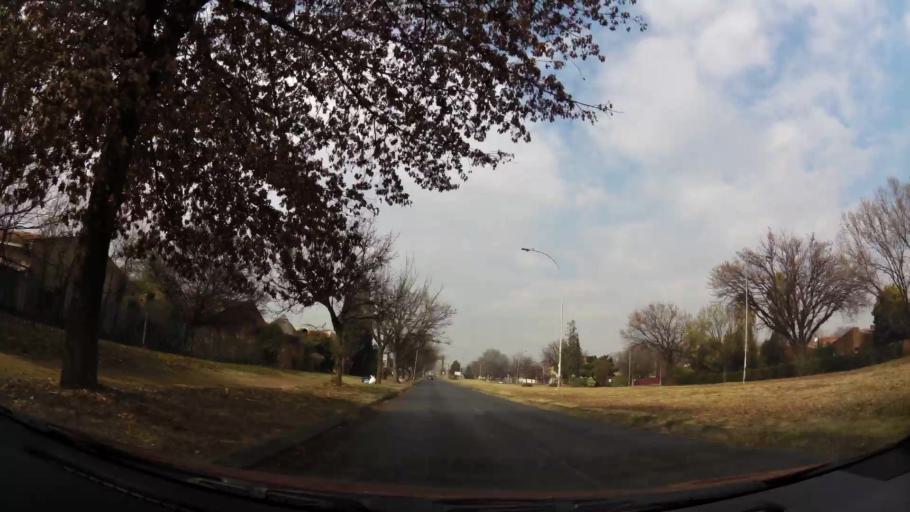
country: ZA
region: Gauteng
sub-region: Sedibeng District Municipality
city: Vanderbijlpark
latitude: -26.6874
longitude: 27.8350
